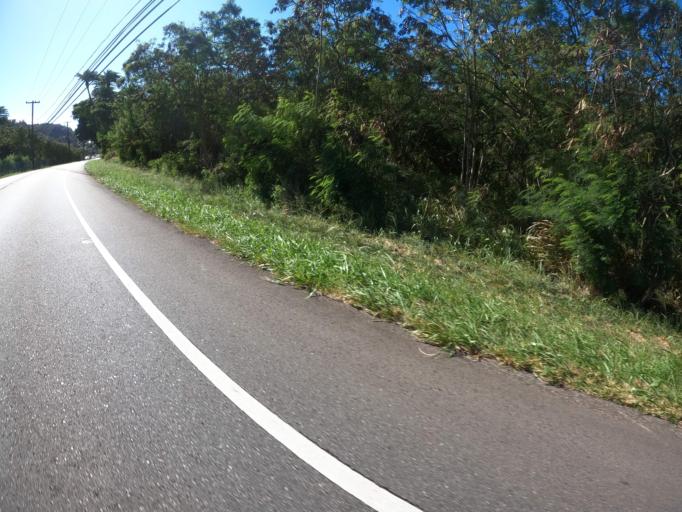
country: US
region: Hawaii
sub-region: Honolulu County
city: Pupukea
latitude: 21.6883
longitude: -158.0223
